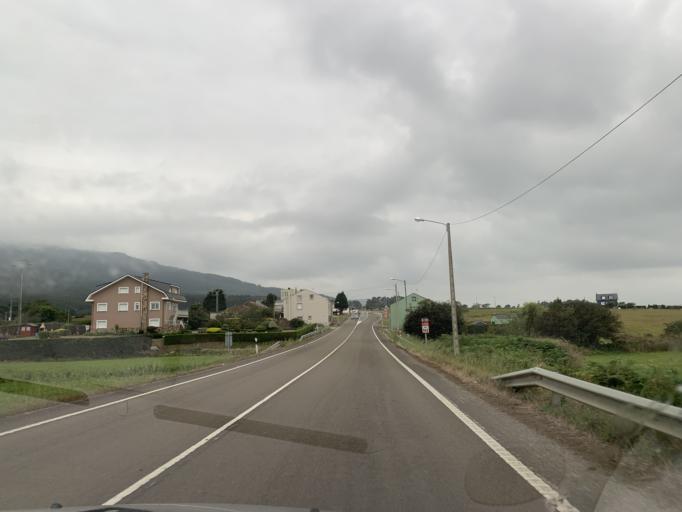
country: ES
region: Galicia
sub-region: Provincia de Lugo
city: Barreiros
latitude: 43.5484
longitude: -7.1472
